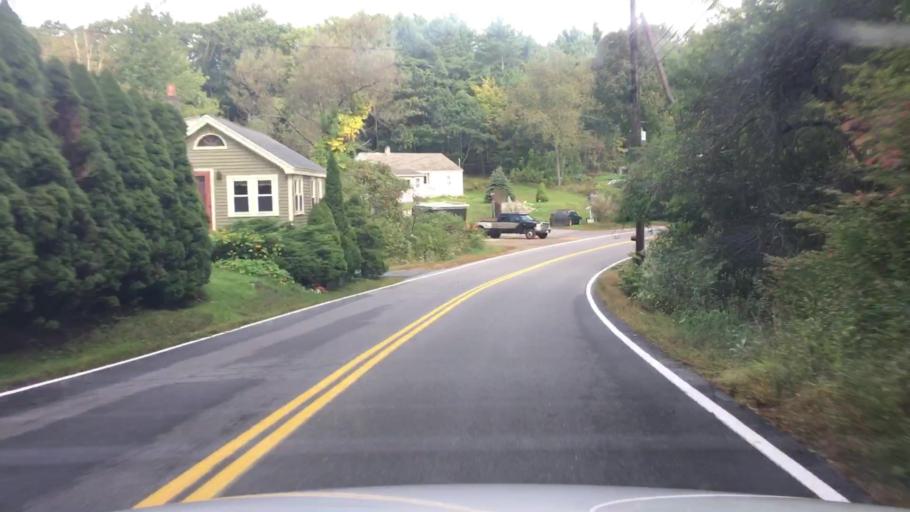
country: US
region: Maine
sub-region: York County
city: Kittery Point
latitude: 43.1026
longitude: -70.6760
